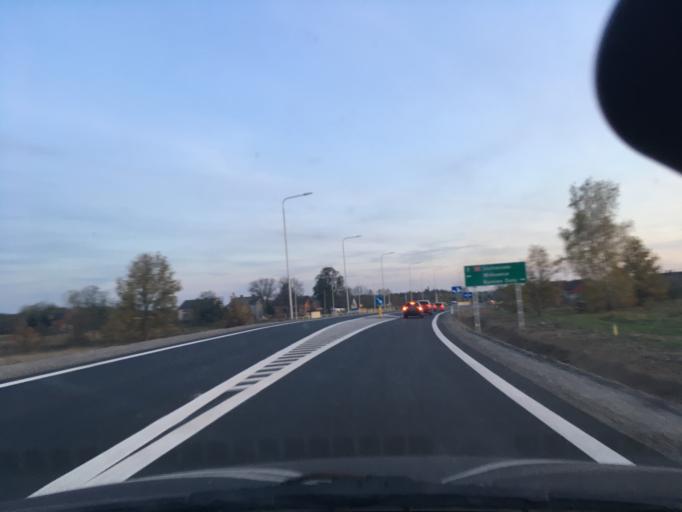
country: PL
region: Masovian Voivodeship
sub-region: Powiat plocki
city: Wyszogrod
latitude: 52.3582
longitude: 20.2074
